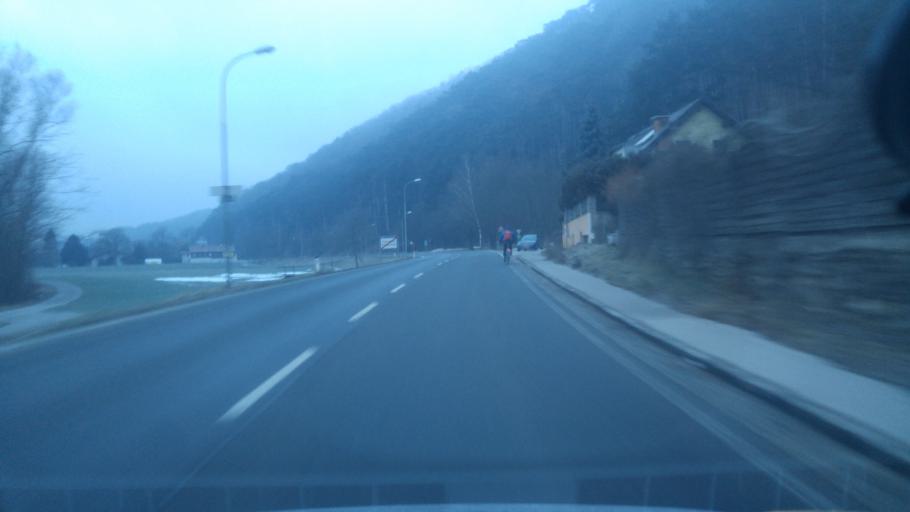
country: AT
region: Lower Austria
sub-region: Politischer Bezirk Baden
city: Weissenbach an der Triesting
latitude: 47.9830
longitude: 16.0615
